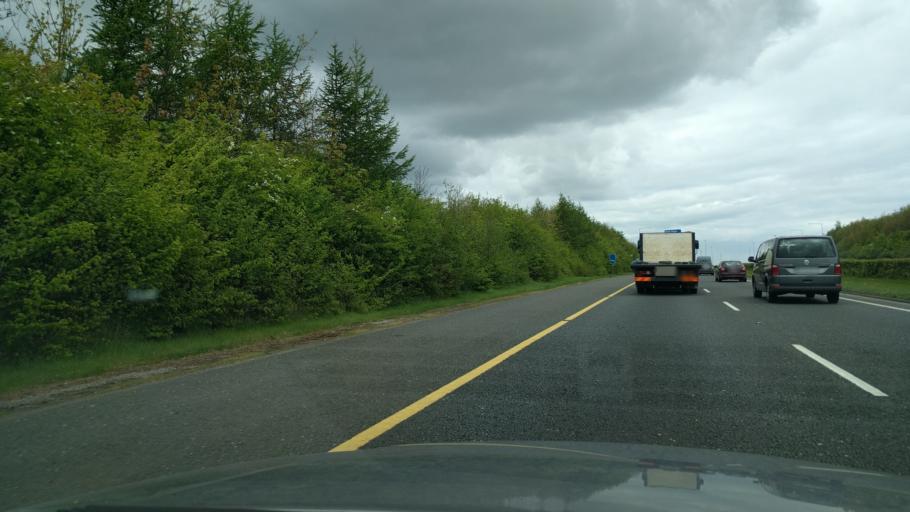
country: IE
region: Leinster
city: Balrothery
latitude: 53.5545
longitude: -6.2158
